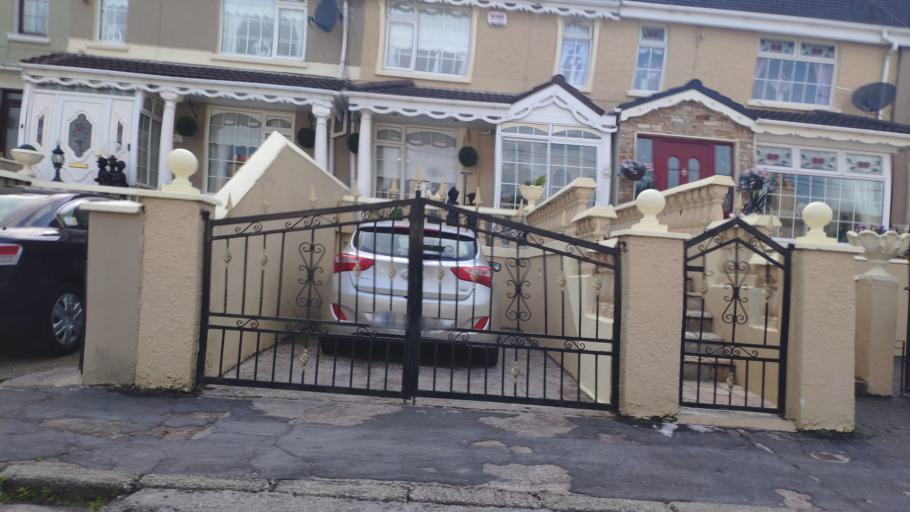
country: IE
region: Munster
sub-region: County Cork
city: Cork
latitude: 51.9051
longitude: -8.4878
